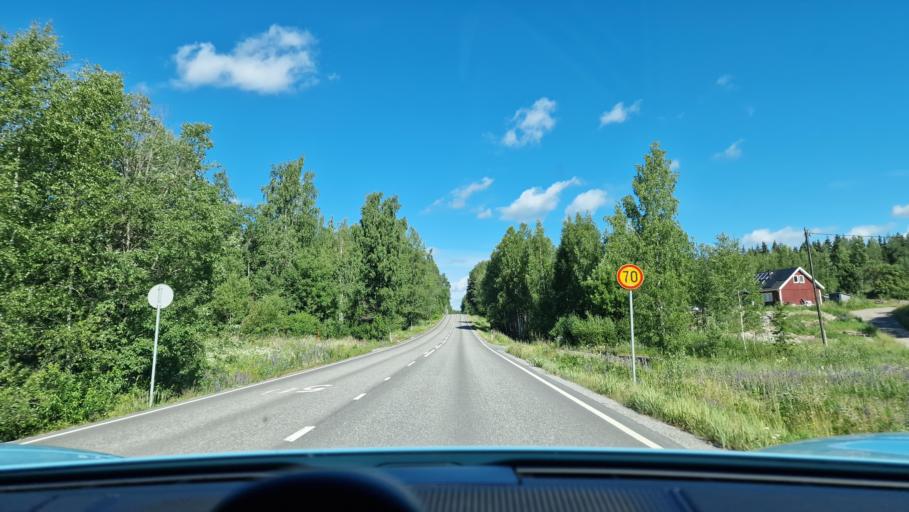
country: FI
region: Pirkanmaa
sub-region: Tampere
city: Orivesi
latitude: 61.6114
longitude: 24.3070
